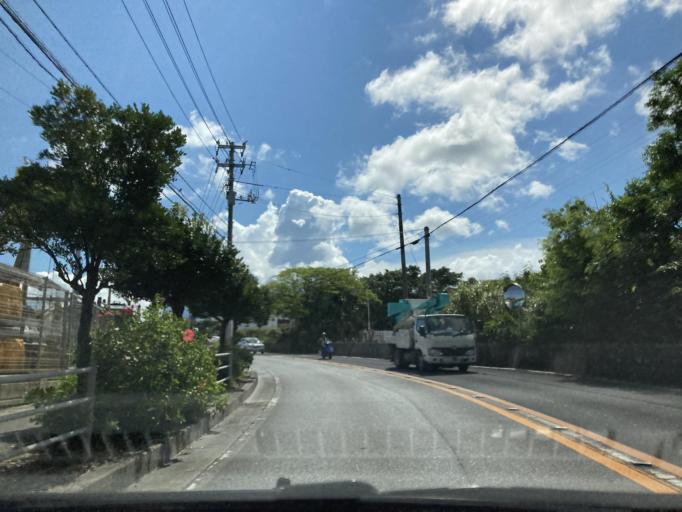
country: JP
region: Okinawa
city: Tomigusuku
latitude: 26.1659
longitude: 127.7211
